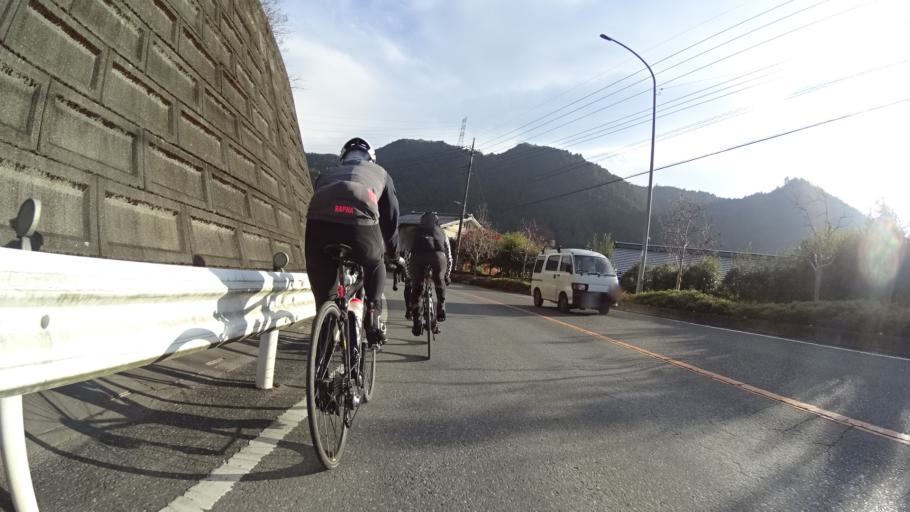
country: JP
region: Tokyo
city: Ome
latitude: 35.8609
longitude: 139.2295
